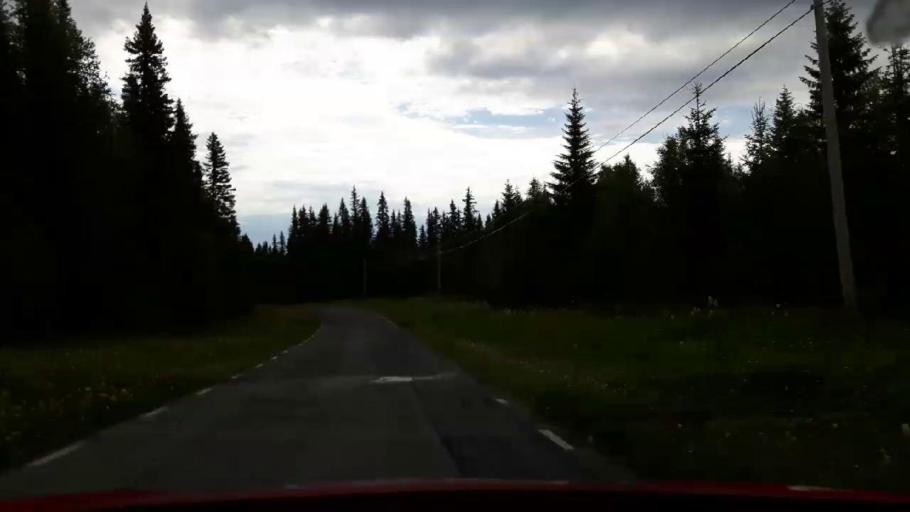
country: SE
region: Jaemtland
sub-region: OEstersunds Kommun
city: Lit
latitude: 63.3687
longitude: 15.1412
